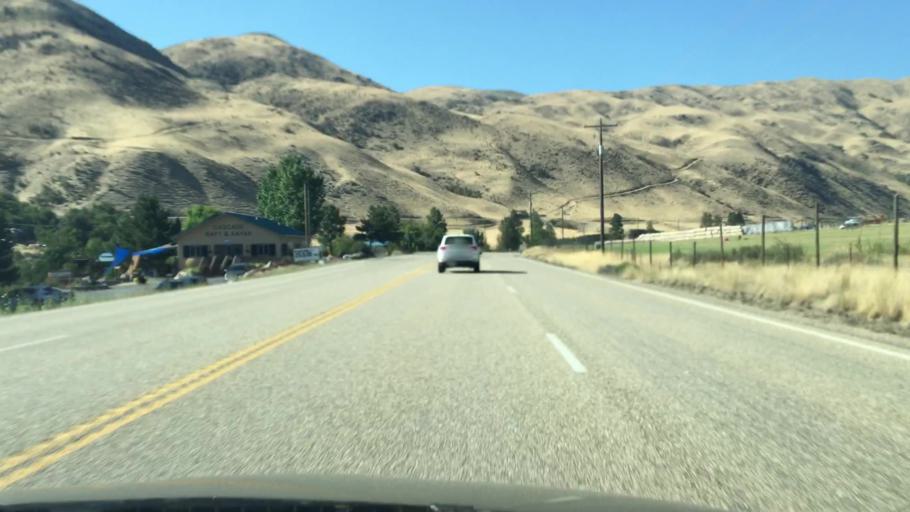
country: US
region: Idaho
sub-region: Gem County
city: Emmett
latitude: 43.9907
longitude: -116.1872
